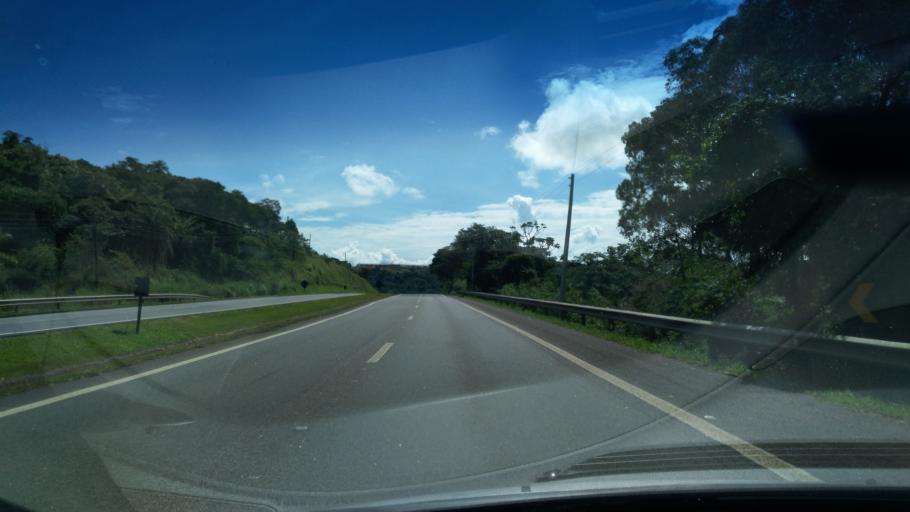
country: BR
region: Sao Paulo
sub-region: Santo Antonio Do Jardim
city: Espirito Santo do Pinhal
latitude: -22.2170
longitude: -46.7858
